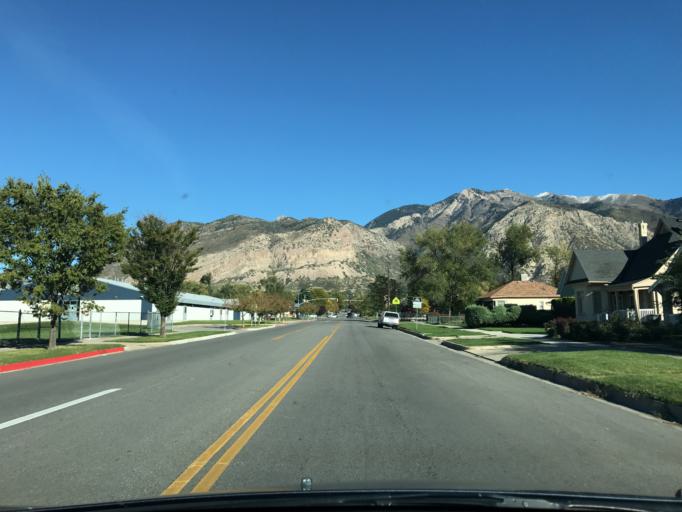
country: US
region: Utah
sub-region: Weber County
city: Ogden
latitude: 41.2184
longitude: -111.9620
